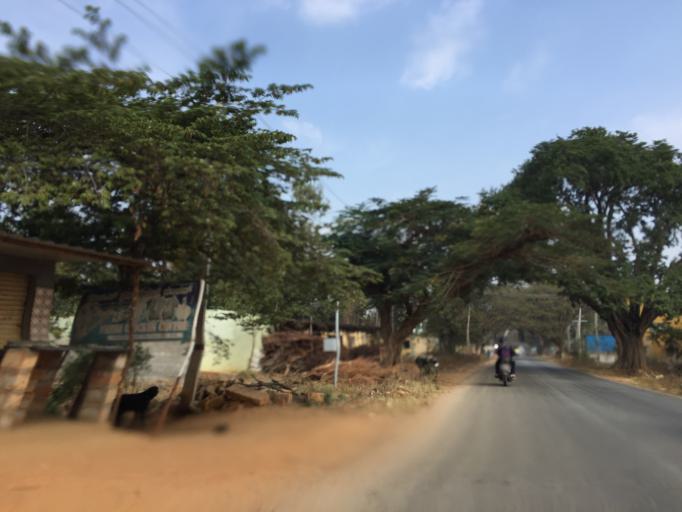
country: IN
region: Karnataka
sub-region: Bangalore Rural
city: Devanhalli
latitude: 13.3282
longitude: 77.6917
